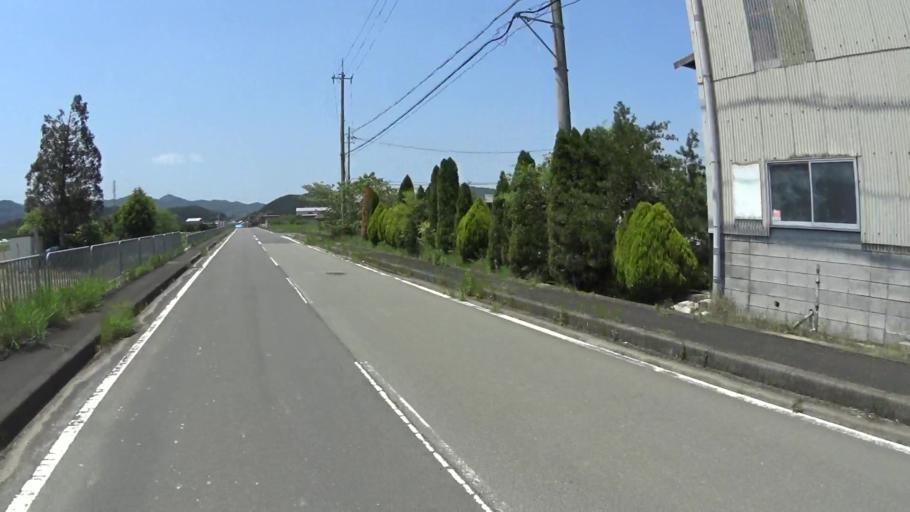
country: JP
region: Kyoto
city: Kameoka
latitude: 35.0766
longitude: 135.5605
